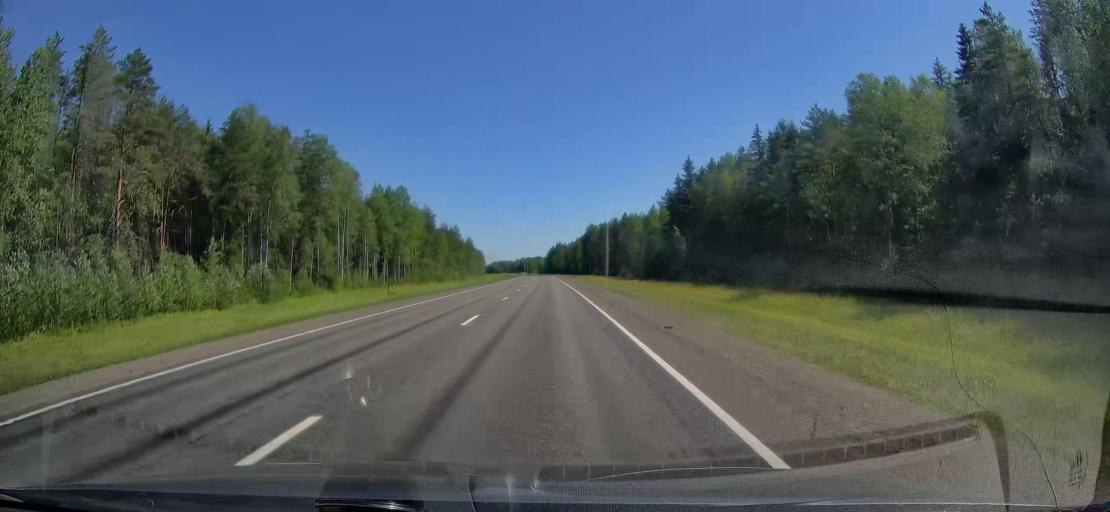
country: RU
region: Tverskaya
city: Ves'yegonsk
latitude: 58.9215
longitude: 37.2059
